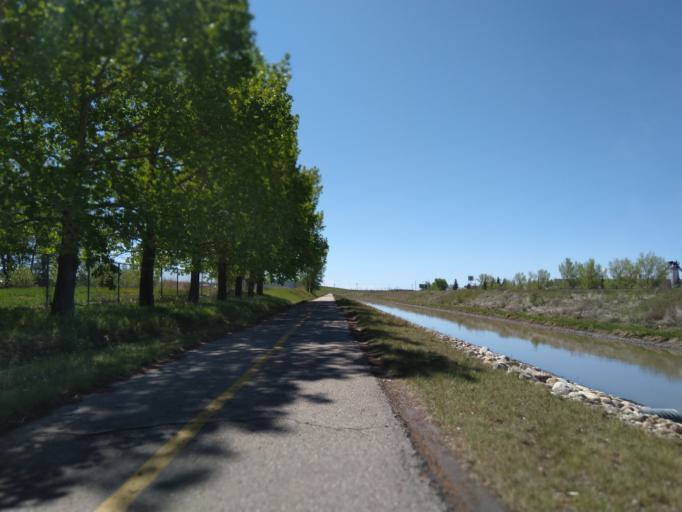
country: CA
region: Alberta
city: Calgary
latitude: 50.9715
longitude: -113.9883
